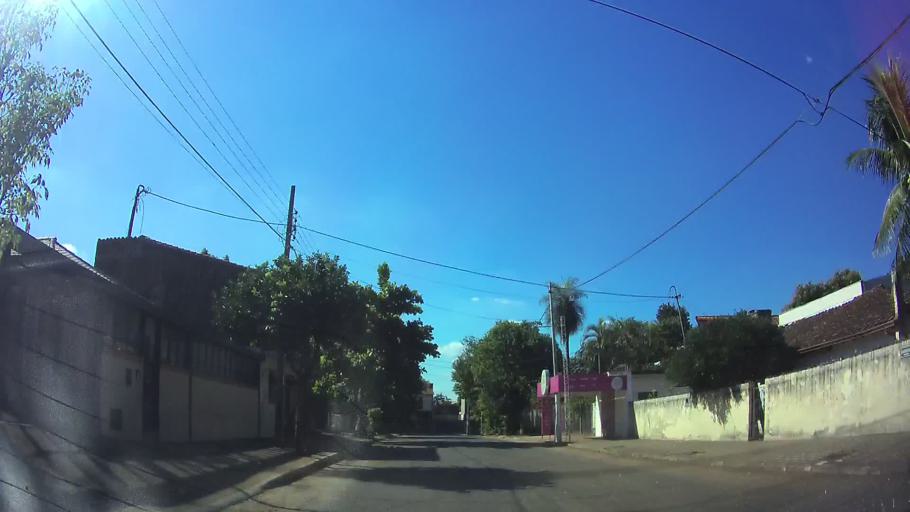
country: PY
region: Central
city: Fernando de la Mora
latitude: -25.3125
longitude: -57.5598
